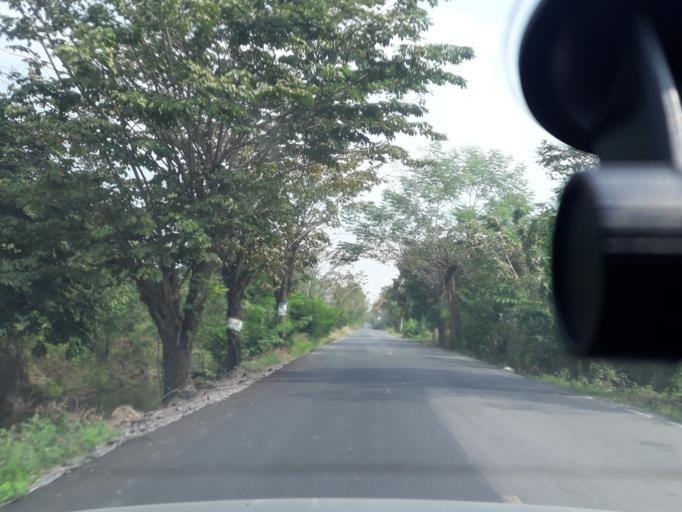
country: TH
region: Pathum Thani
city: Nong Suea
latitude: 14.1968
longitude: 100.8782
